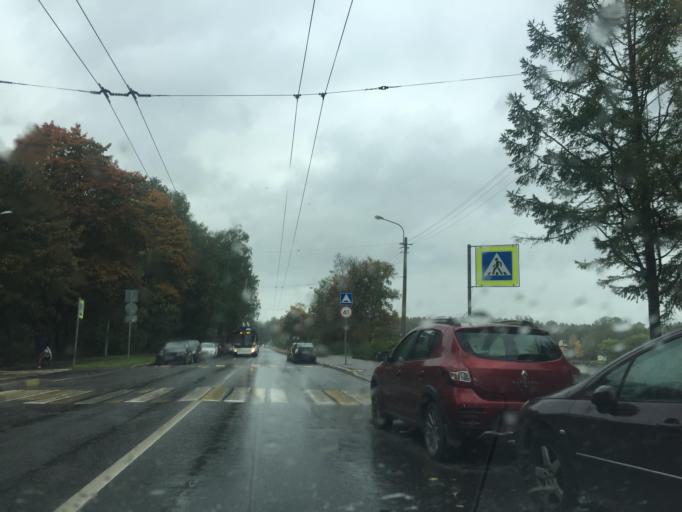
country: RU
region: St.-Petersburg
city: Sosnovka
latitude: 60.0102
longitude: 30.3587
